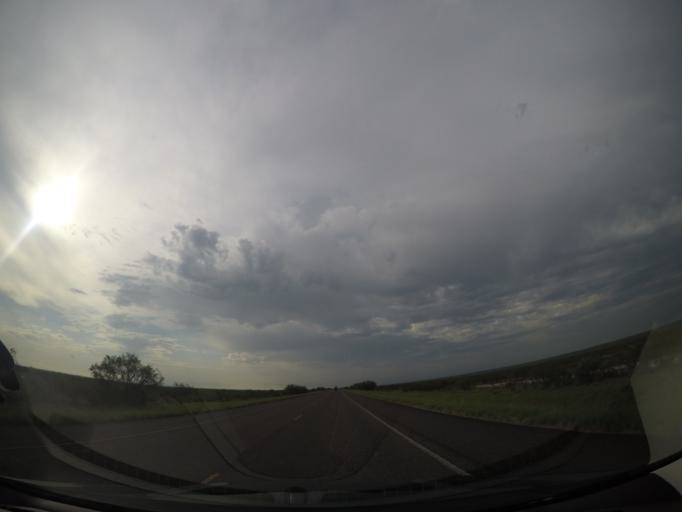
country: US
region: Texas
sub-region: Terrell County
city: Sanderson
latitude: 29.9235
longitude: -101.9226
